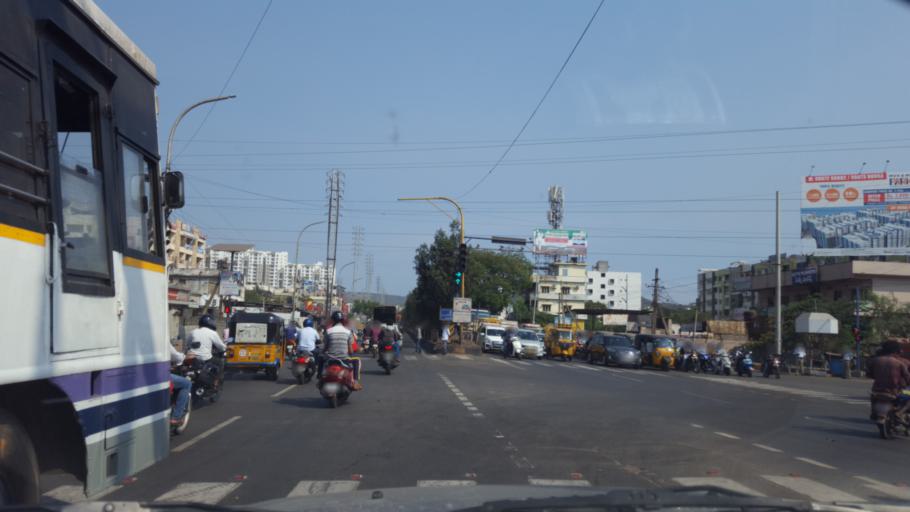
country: IN
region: Andhra Pradesh
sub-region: Vishakhapatnam
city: Visakhapatnam
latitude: 17.6835
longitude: 83.1935
